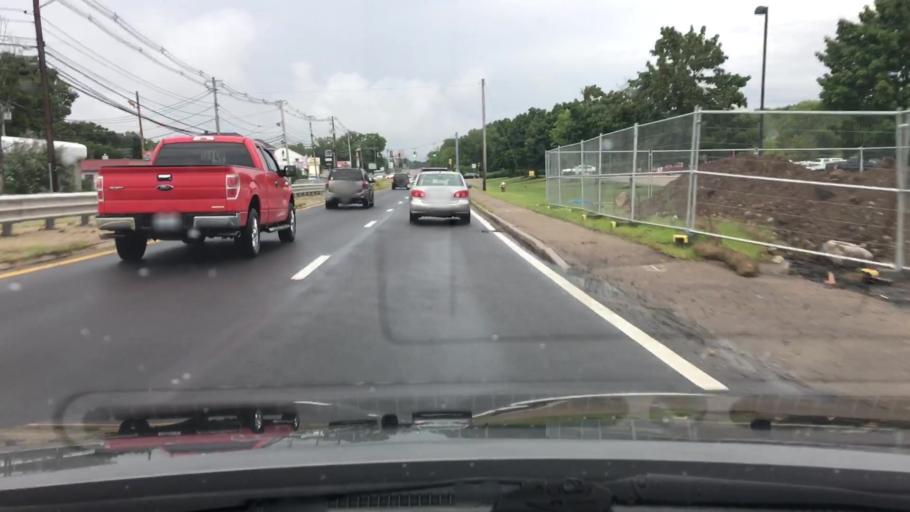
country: US
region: Massachusetts
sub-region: Norfolk County
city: Plainville
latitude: 41.9537
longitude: -71.3439
